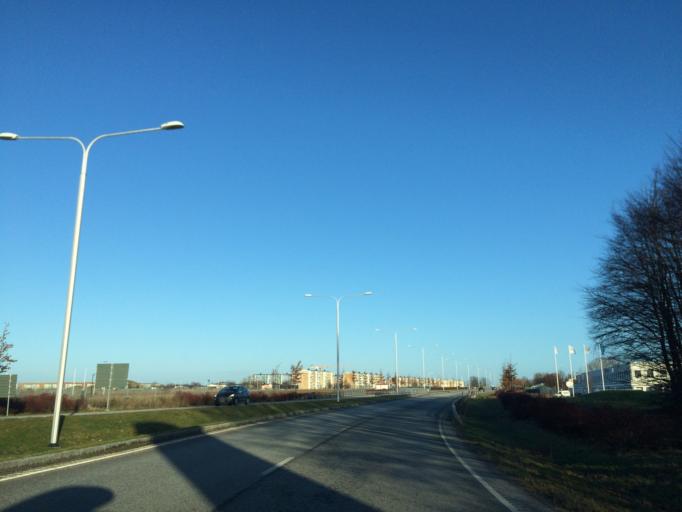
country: SE
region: Skane
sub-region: Malmo
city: Malmoe
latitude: 55.5641
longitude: 12.9850
